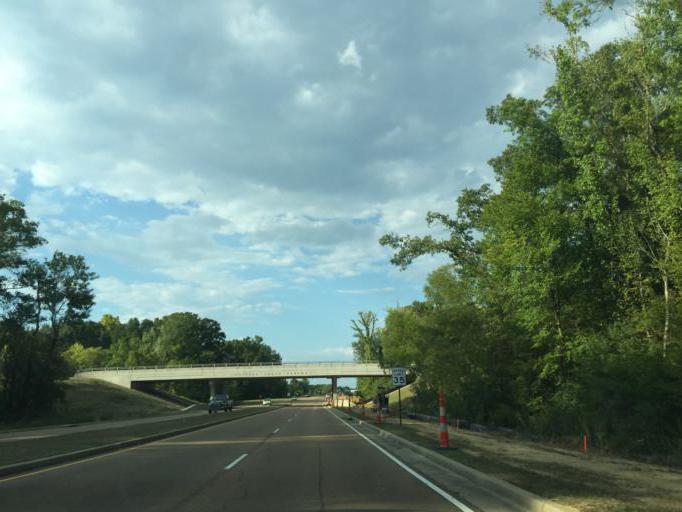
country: US
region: Mississippi
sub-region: Madison County
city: Ridgeland
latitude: 32.4260
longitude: -90.1063
